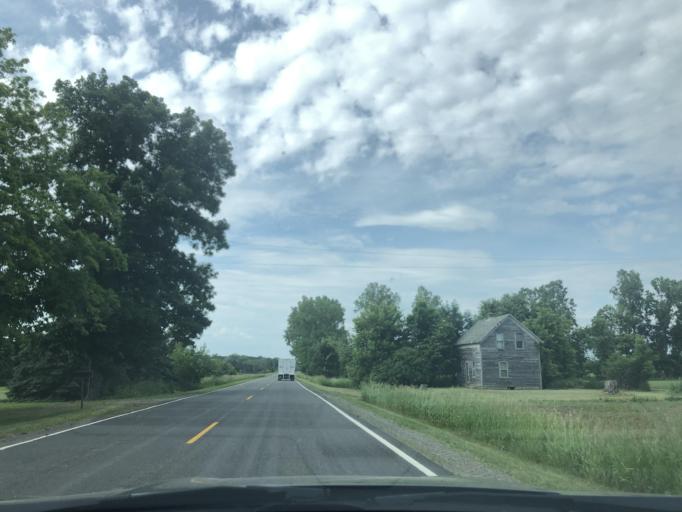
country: US
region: Michigan
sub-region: Clinton County
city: Saint Johns
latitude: 42.9660
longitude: -84.4837
